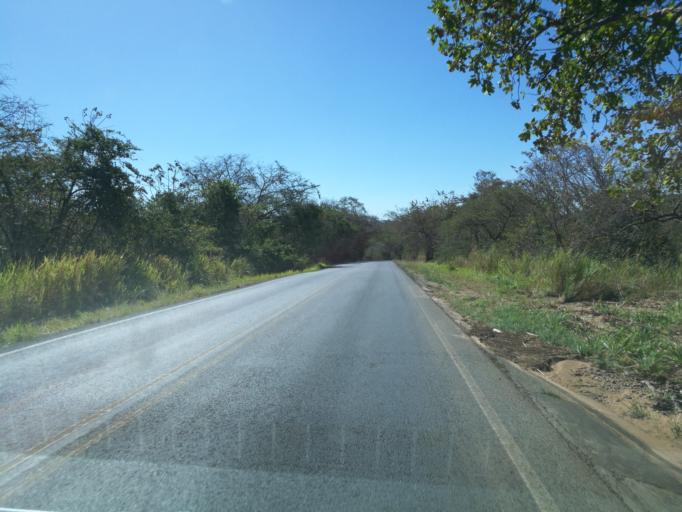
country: CR
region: Puntarenas
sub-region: Canton Central de Puntarenas
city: Puntarenas
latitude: 10.0916
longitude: -84.8540
